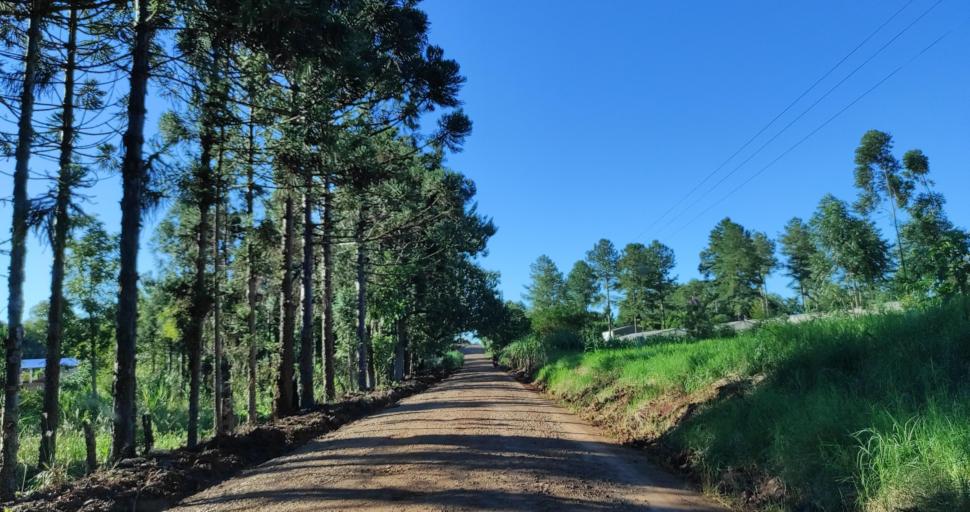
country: AR
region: Misiones
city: Puerto Rico
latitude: -26.8272
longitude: -55.0011
